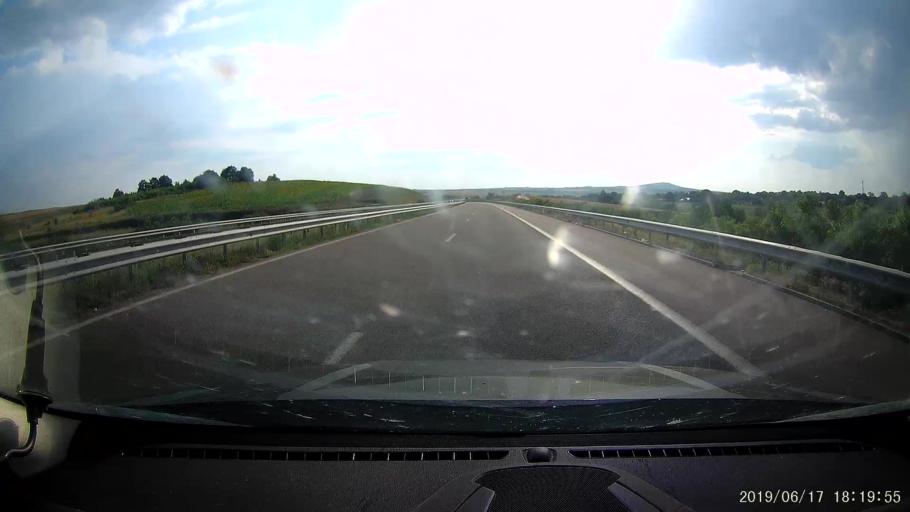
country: BG
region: Khaskovo
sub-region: Obshtina Simeonovgrad
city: Simeonovgrad
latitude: 41.9629
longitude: 25.8308
